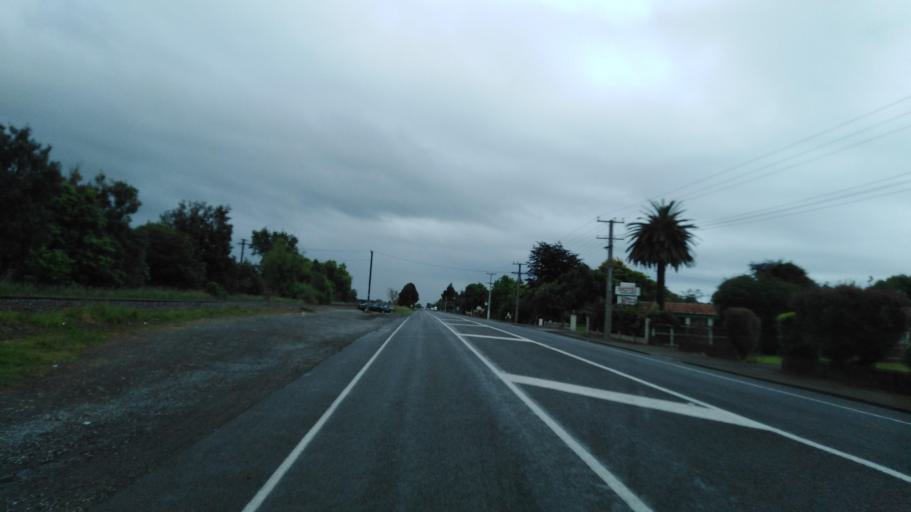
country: NZ
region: Manawatu-Wanganui
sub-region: Horowhenua District
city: Levin
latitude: -40.6396
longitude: 175.2691
